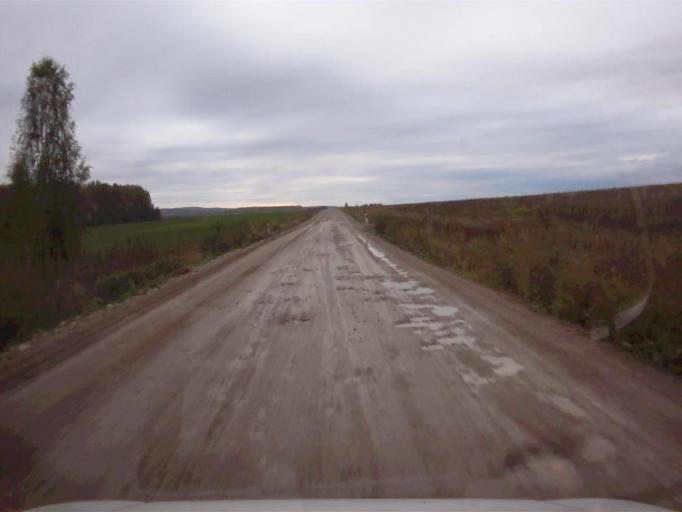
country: RU
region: Sverdlovsk
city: Mikhaylovsk
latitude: 56.1783
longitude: 59.2027
